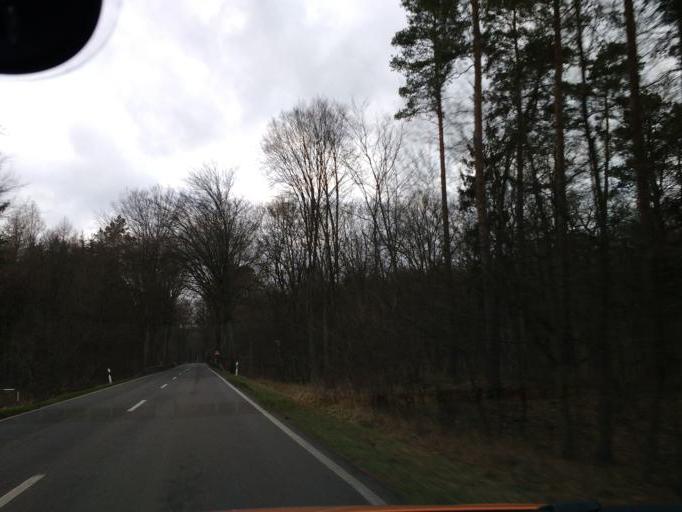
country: DE
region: Brandenburg
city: Strausberg
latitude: 52.6482
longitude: 13.9124
